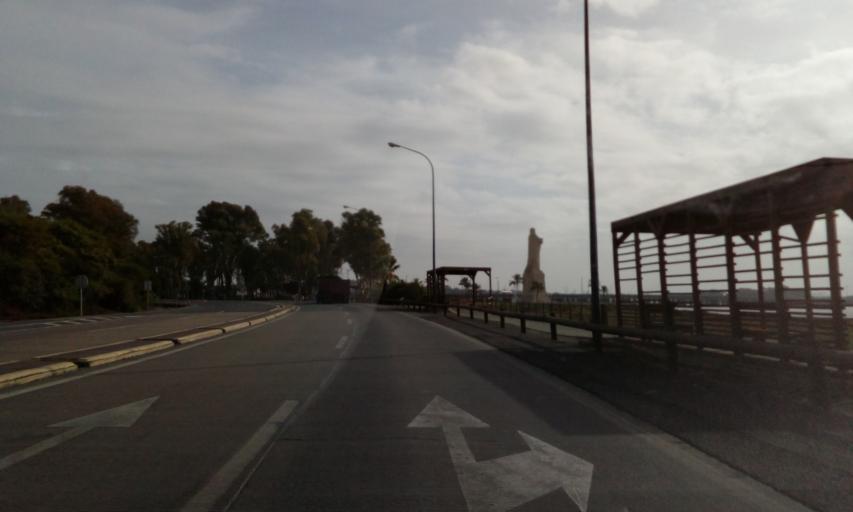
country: ES
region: Andalusia
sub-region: Provincia de Huelva
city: Punta Umbria
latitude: 37.2141
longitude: -6.9433
